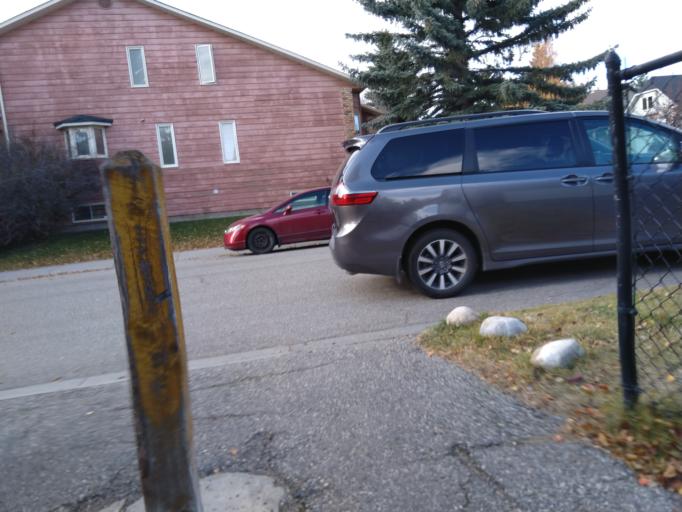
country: CA
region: Alberta
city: Calgary
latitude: 51.1340
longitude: -114.1537
